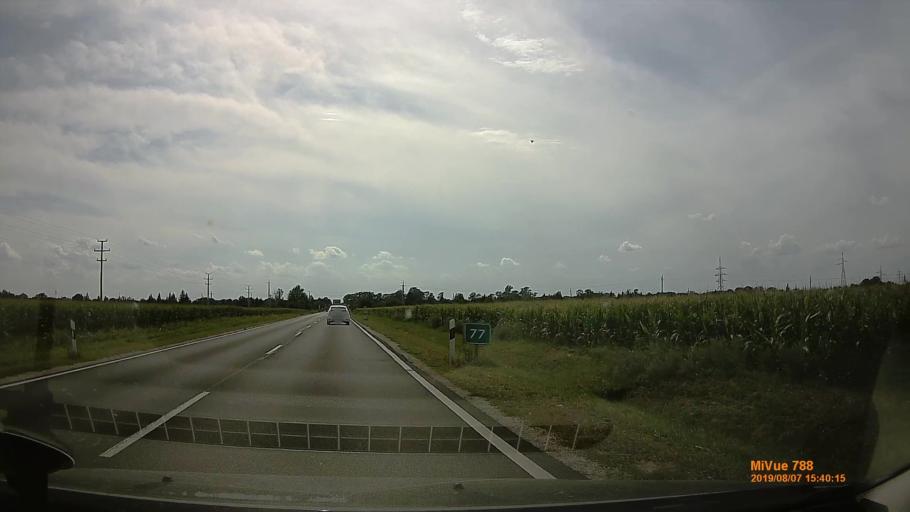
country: HU
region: Vas
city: Szombathely
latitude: 47.2151
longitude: 16.6521
